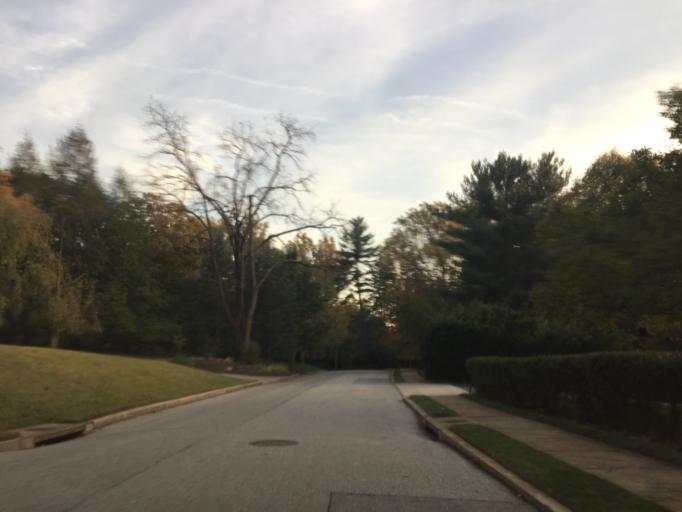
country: US
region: Maryland
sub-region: Baltimore County
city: Towson
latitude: 39.3495
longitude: -76.6268
